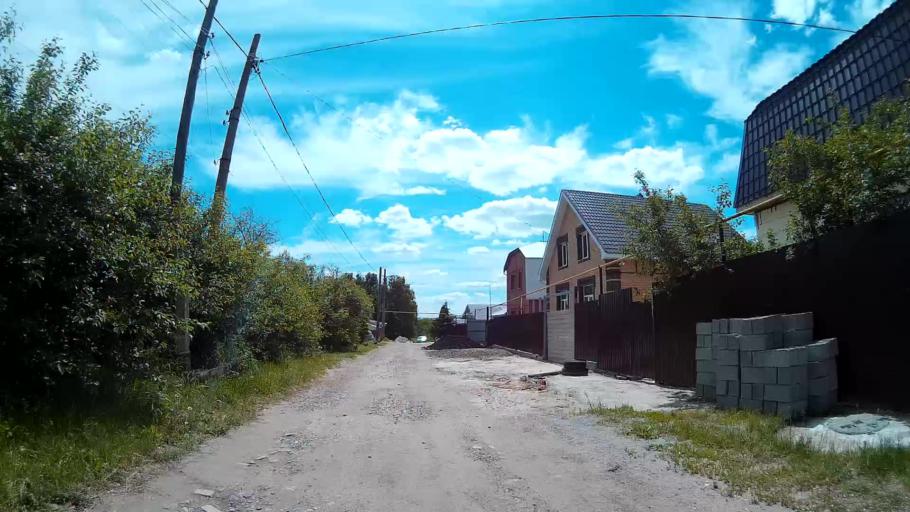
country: RU
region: Ulyanovsk
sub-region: Ulyanovskiy Rayon
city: Ulyanovsk
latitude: 54.2768
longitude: 48.3452
